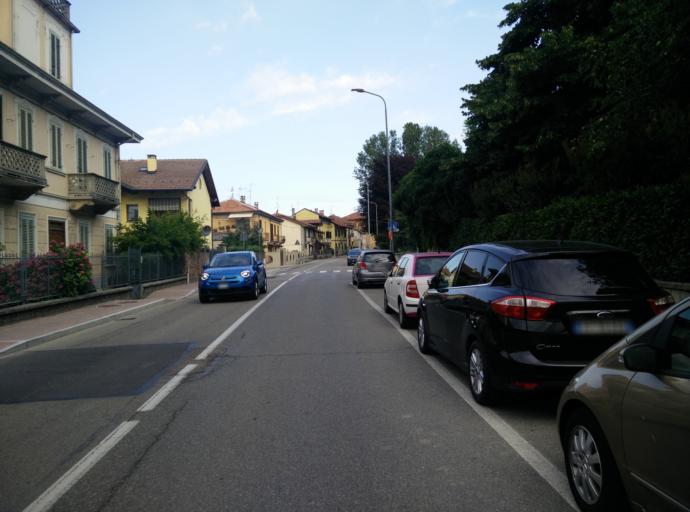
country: IT
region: Piedmont
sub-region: Provincia di Torino
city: Moncalieri
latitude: 44.9996
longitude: 7.7043
